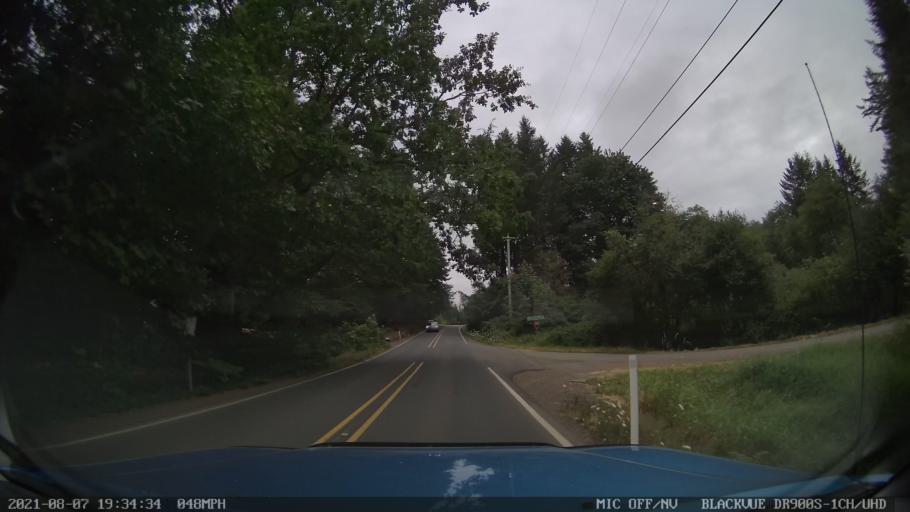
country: US
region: Oregon
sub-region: Linn County
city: Lyons
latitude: 44.9191
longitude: -122.6561
